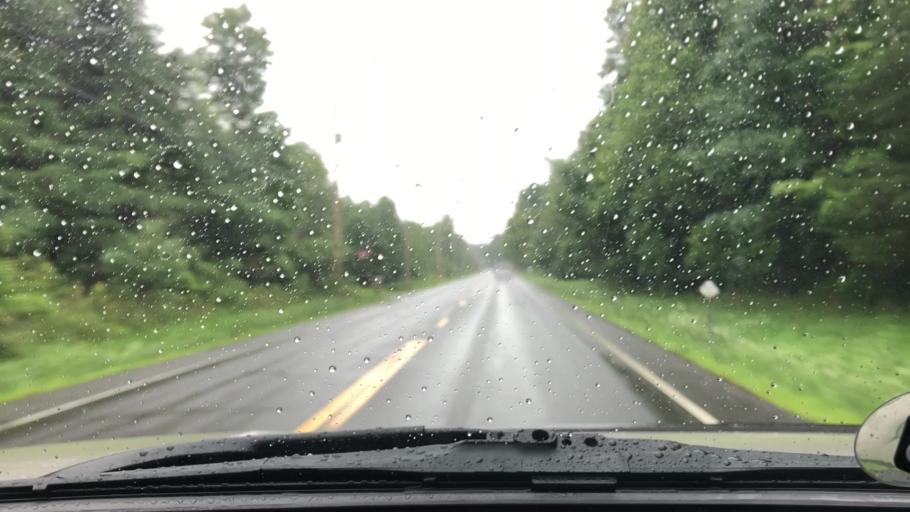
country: US
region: New York
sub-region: Greene County
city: Cairo
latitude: 42.2751
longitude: -73.9780
